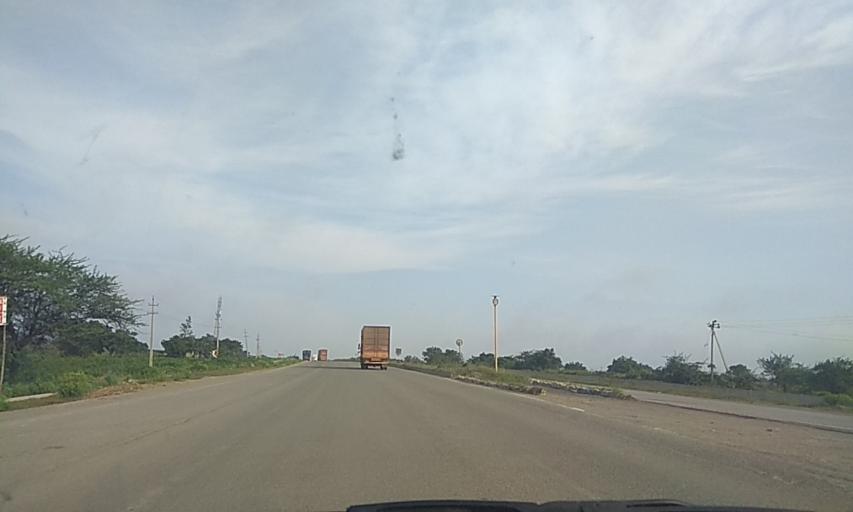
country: IN
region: Karnataka
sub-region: Haveri
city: Byadgi
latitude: 14.7007
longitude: 75.5231
